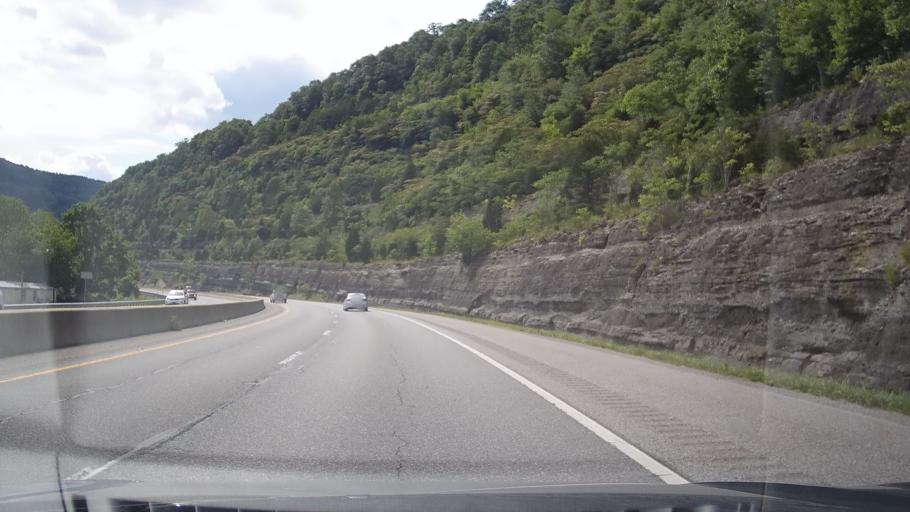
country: US
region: Kentucky
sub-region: Pike County
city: Coal Run Village
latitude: 37.5583
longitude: -82.6327
